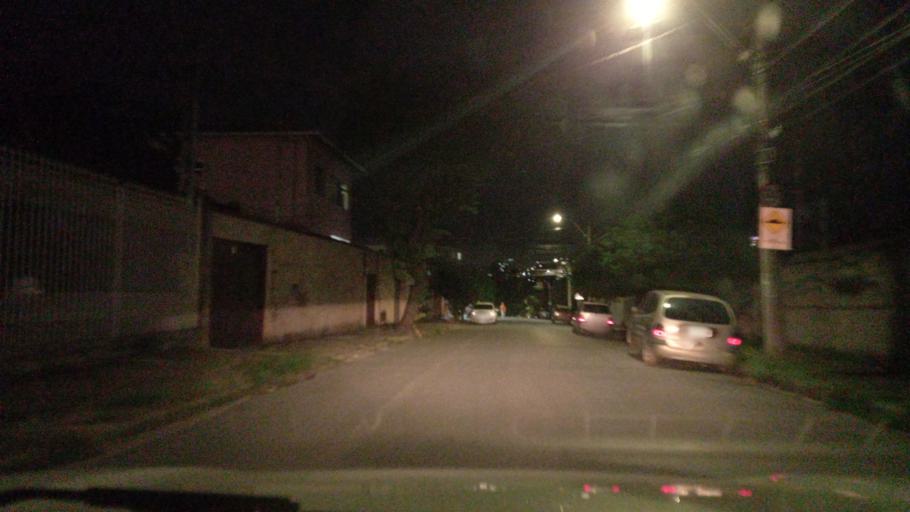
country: BR
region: Minas Gerais
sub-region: Belo Horizonte
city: Belo Horizonte
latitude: -19.8807
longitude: -43.9380
